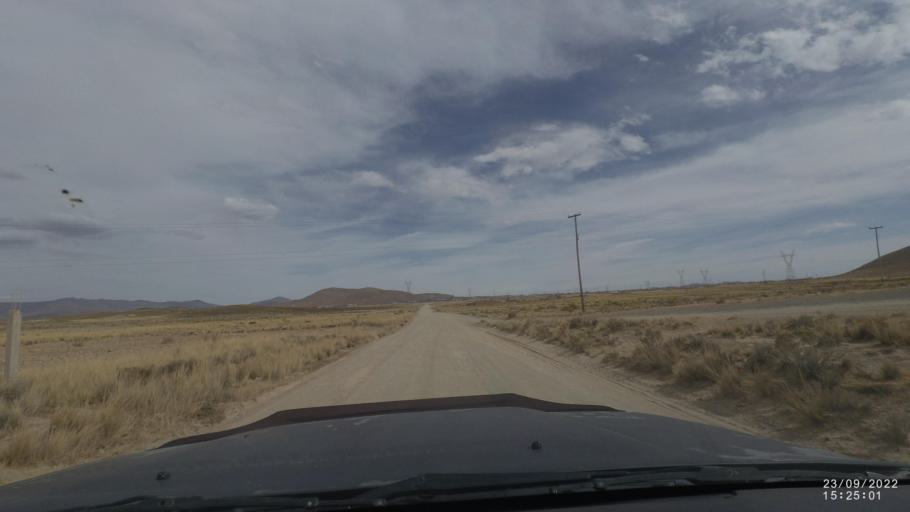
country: BO
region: Oruro
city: Oruro
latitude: -17.9408
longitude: -67.0401
